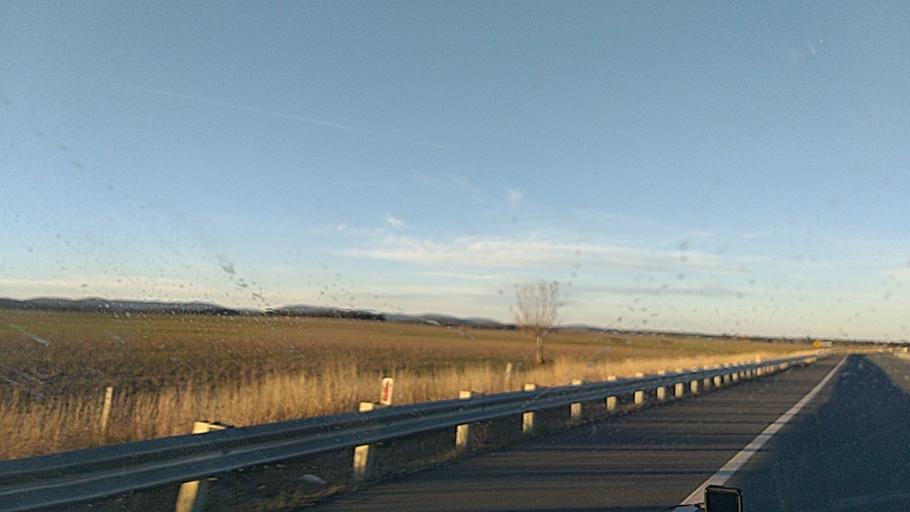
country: AU
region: New South Wales
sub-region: Goulburn Mulwaree
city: Goulburn
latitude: -34.8503
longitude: 149.5554
